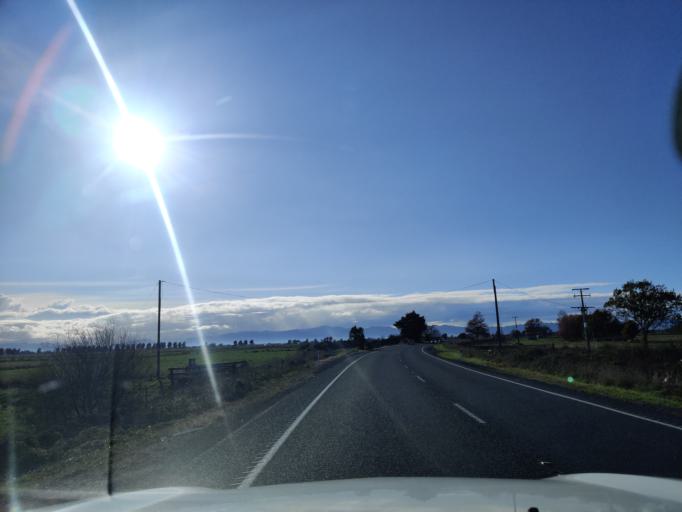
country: NZ
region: Waikato
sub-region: Hauraki District
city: Ngatea
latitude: -37.2767
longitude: 175.4624
